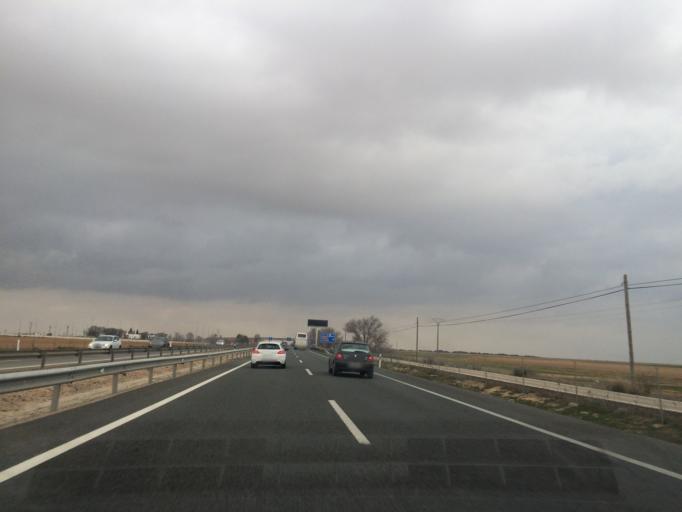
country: ES
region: Castille-La Mancha
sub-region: Province of Toledo
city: Tembleque
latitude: 39.6441
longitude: -3.5165
